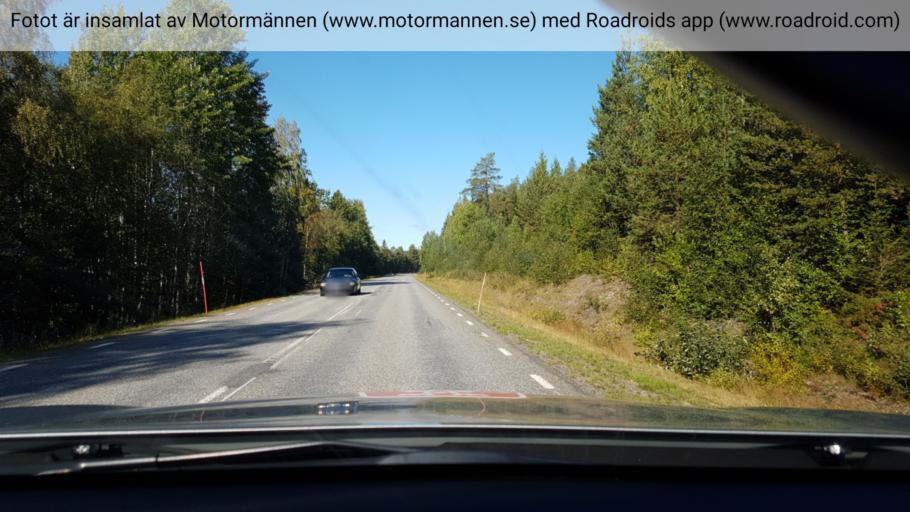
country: SE
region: Vaesterbotten
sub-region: Norsjo Kommun
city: Norsjoe
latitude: 64.9361
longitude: 19.3843
